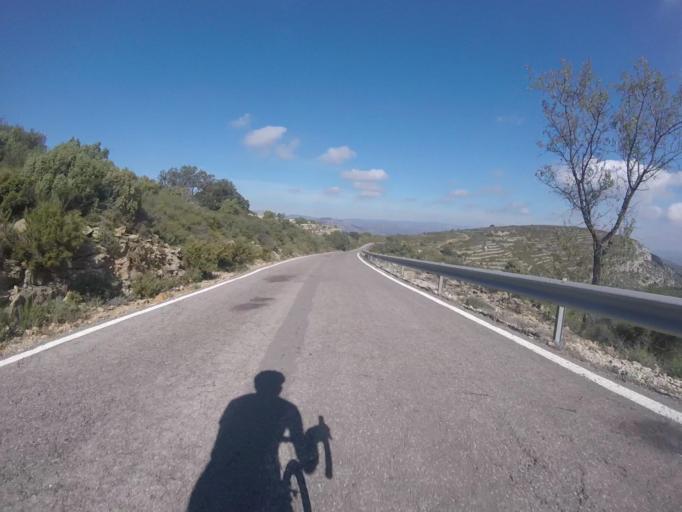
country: ES
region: Valencia
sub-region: Provincia de Castello
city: Albocasser
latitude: 40.3425
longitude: 0.0495
